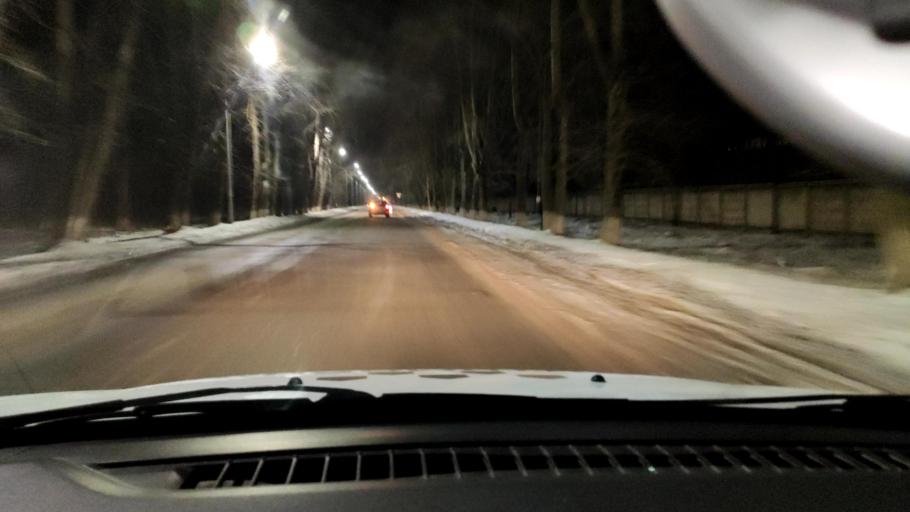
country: RU
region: Perm
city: Kultayevo
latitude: 57.9784
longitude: 55.9150
